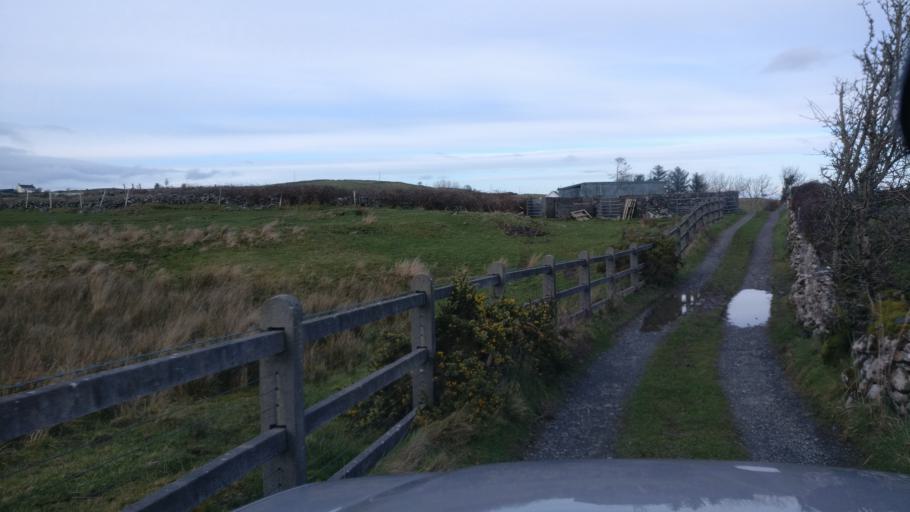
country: IE
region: Connaught
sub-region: County Galway
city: Oughterard
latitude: 53.5262
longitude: -9.3763
